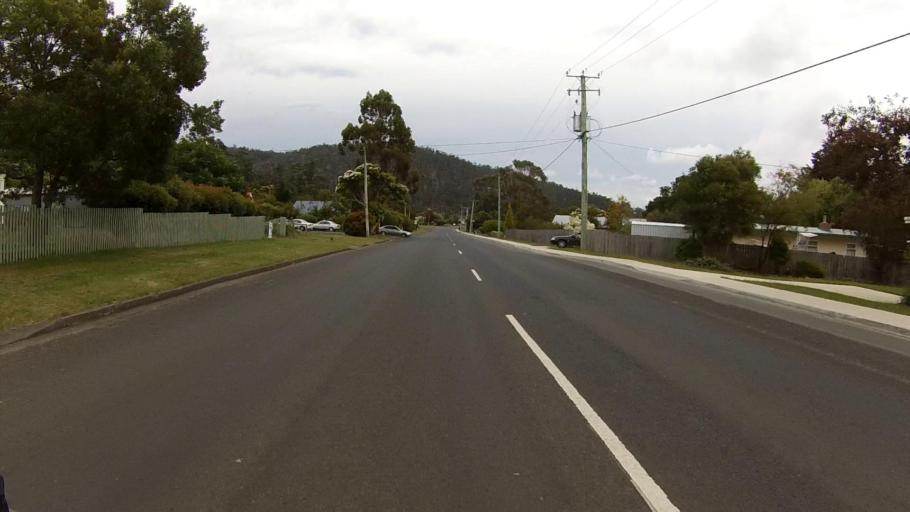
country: AU
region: Tasmania
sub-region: Sorell
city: Sorell
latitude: -42.5629
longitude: 147.8728
